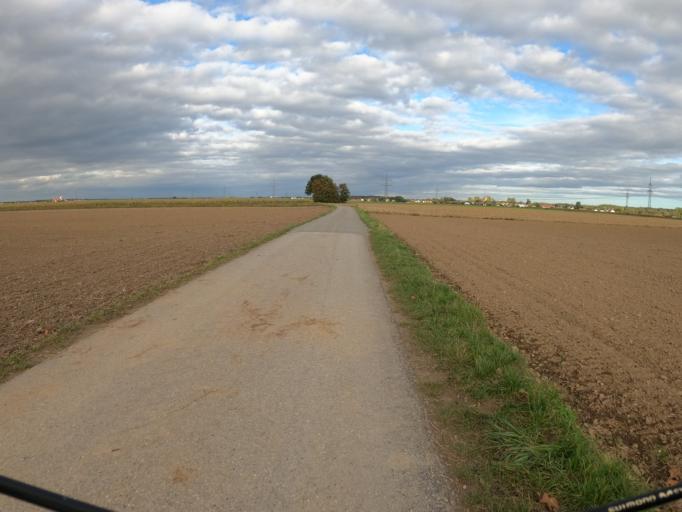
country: DE
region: Bavaria
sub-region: Swabia
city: Nersingen
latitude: 48.4090
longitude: 10.1188
